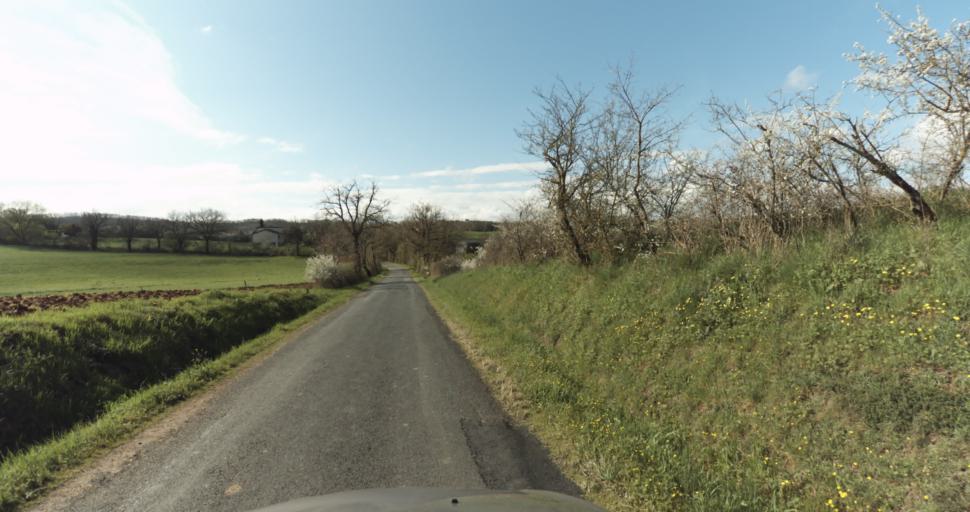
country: FR
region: Midi-Pyrenees
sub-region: Departement du Tarn
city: Puygouzon
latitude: 43.8784
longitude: 2.1813
